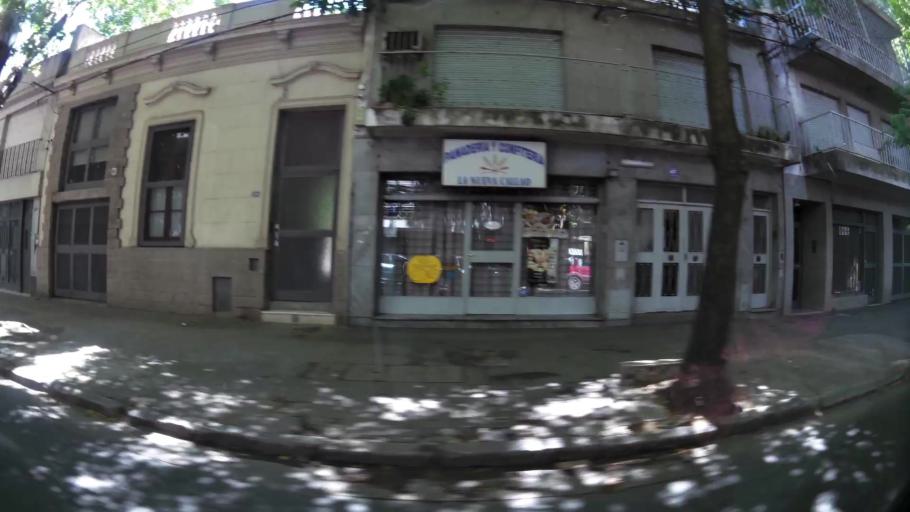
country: AR
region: Santa Fe
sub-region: Departamento de Rosario
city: Rosario
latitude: -32.9445
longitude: -60.6606
